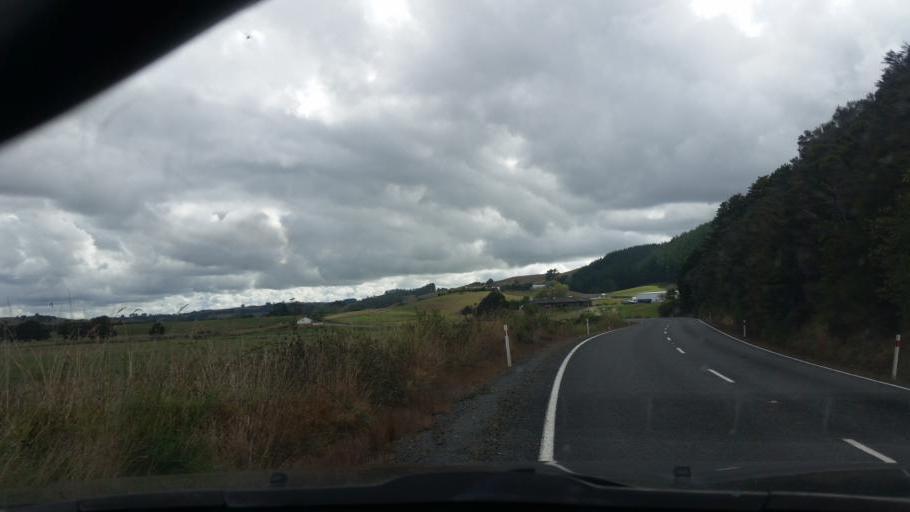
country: NZ
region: Northland
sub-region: Whangarei
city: Ruakaka
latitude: -35.9679
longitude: 174.2904
